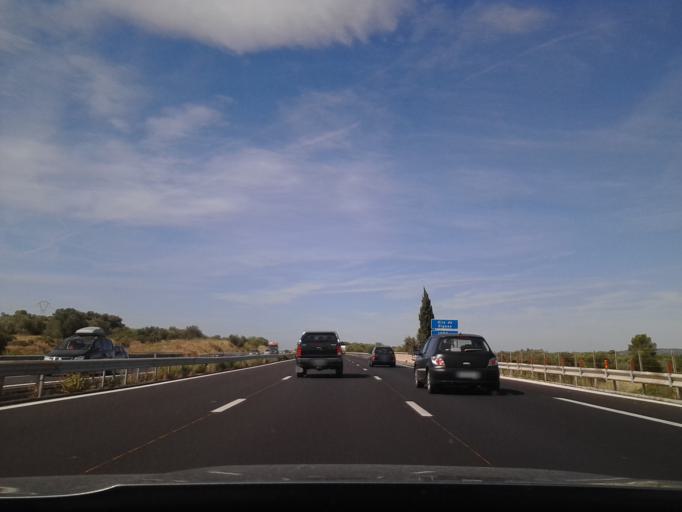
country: FR
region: Languedoc-Roussillon
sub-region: Departement de l'Herault
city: Gigean
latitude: 43.5025
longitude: 3.7301
